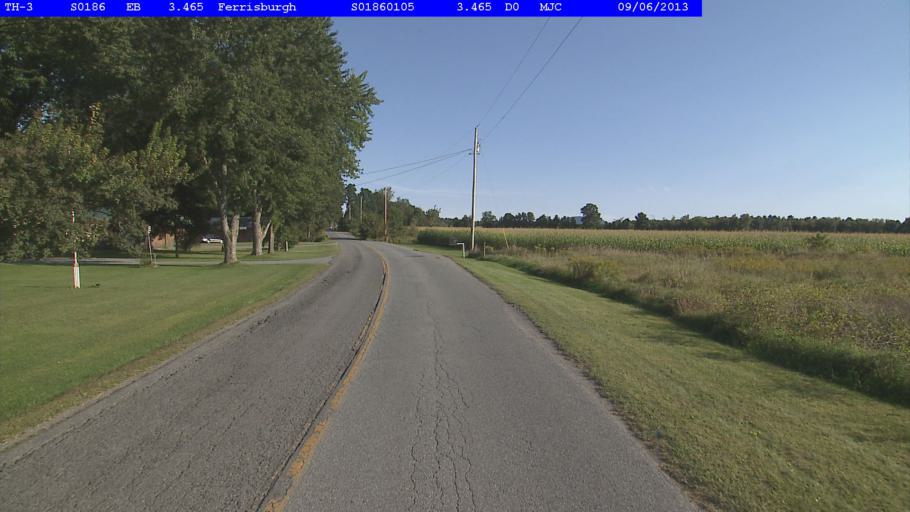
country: US
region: Vermont
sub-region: Addison County
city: Vergennes
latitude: 44.1768
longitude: -73.3077
